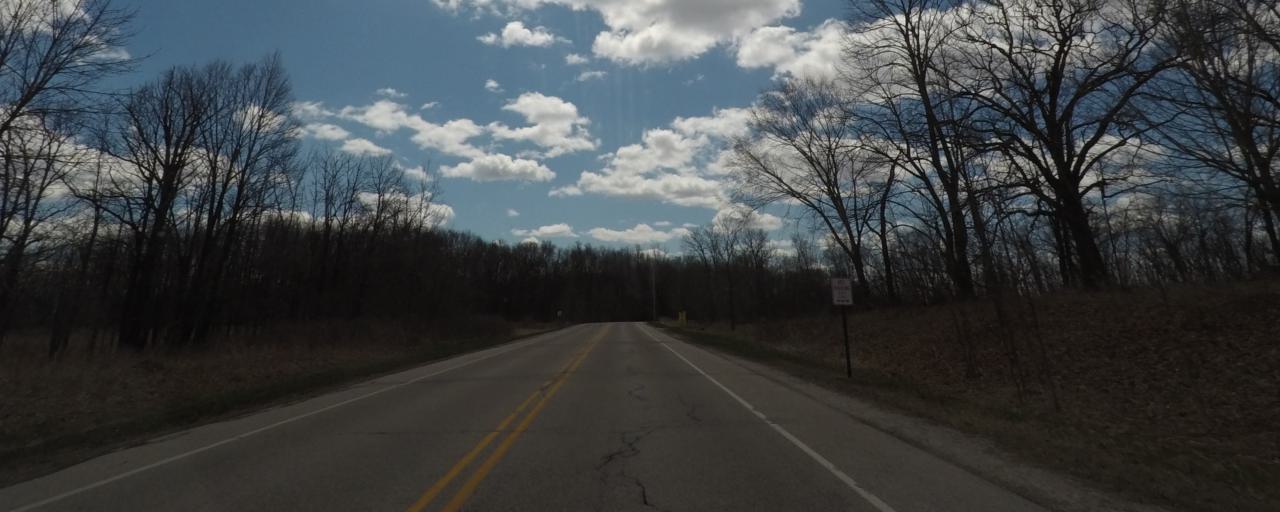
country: US
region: Wisconsin
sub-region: Waukesha County
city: Brookfield
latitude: 43.0835
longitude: -88.1585
